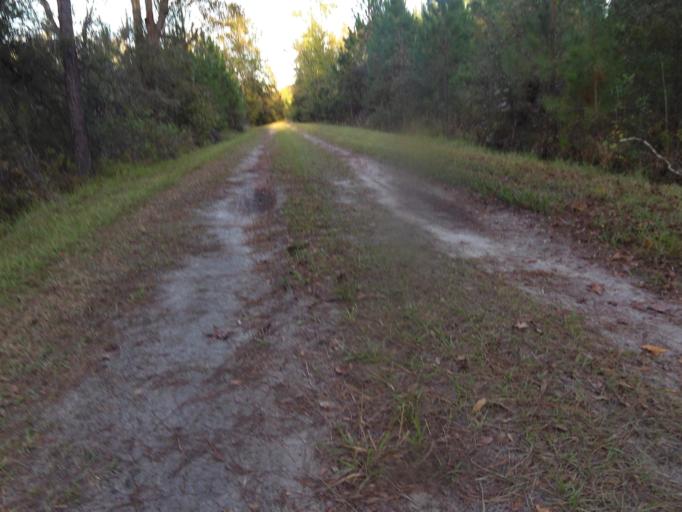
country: US
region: Florida
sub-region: Putnam County
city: Palatka
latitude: 29.6765
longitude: -81.7506
